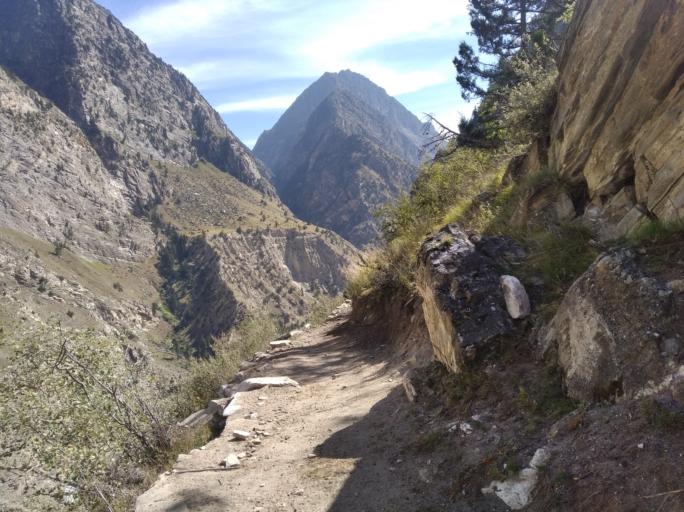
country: NP
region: Western Region
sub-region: Dhawalagiri Zone
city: Jomsom
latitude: 28.8966
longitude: 83.0541
